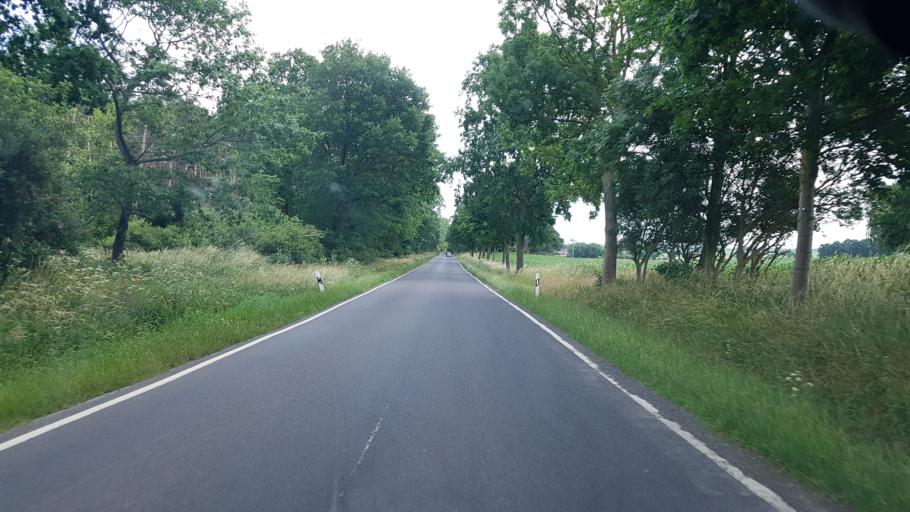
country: DE
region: Mecklenburg-Vorpommern
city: Strasburg
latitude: 53.4076
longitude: 13.7525
